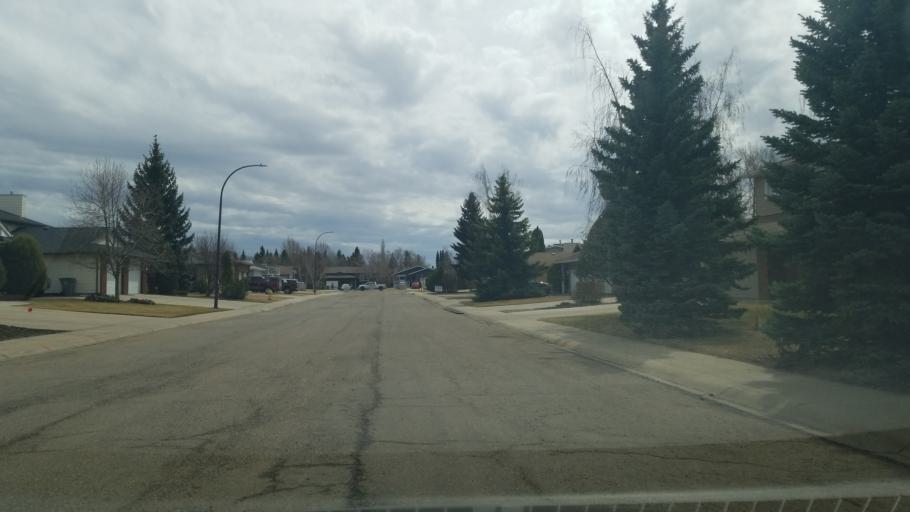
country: CA
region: Saskatchewan
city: Lloydminster
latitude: 53.2727
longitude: -110.0259
